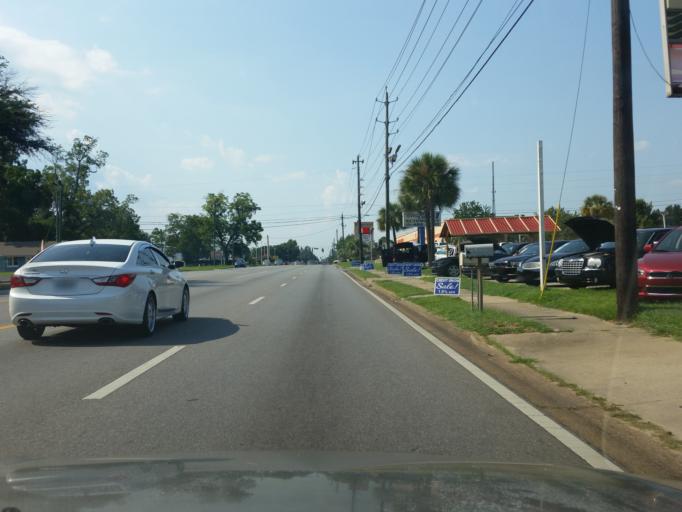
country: US
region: Florida
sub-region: Escambia County
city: Brent
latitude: 30.4692
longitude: -87.2539
